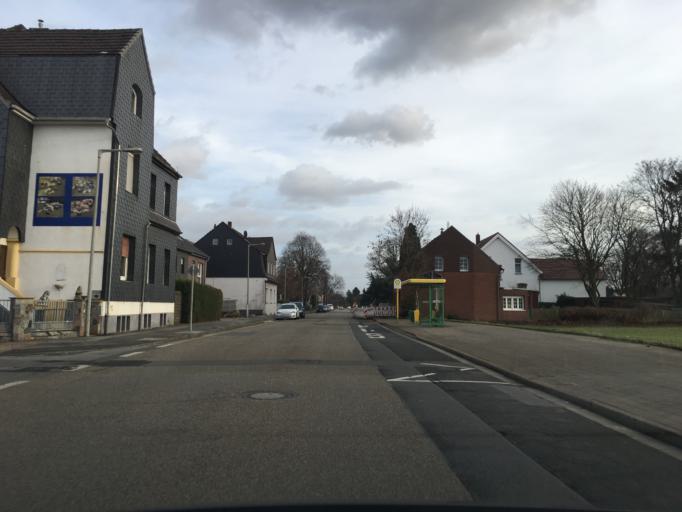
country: DE
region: North Rhine-Westphalia
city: Meiderich
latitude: 51.5174
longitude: 6.7921
